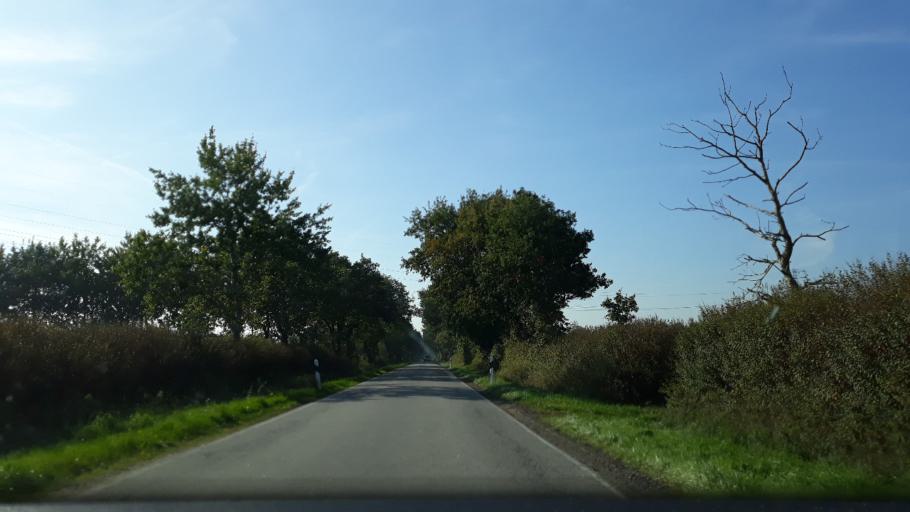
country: DE
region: Schleswig-Holstein
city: Alt Bennebek
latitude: 54.3991
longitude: 9.4197
